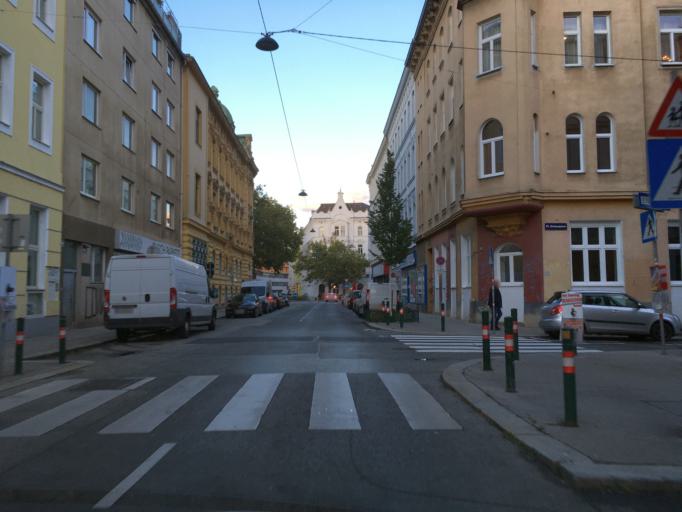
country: AT
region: Vienna
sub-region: Wien Stadt
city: Vienna
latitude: 48.1859
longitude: 16.3306
